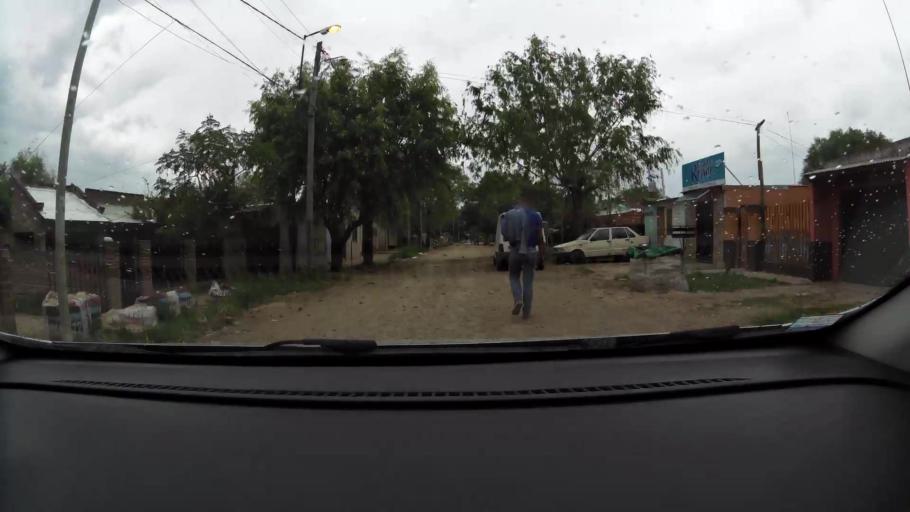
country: AR
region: Buenos Aires
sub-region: Partido de Zarate
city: Zarate
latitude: -34.1161
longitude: -59.0408
